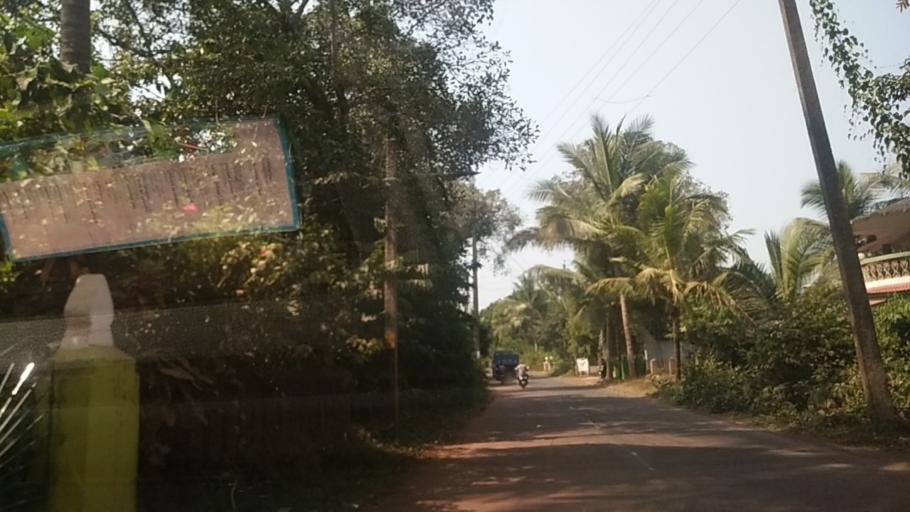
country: IN
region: Goa
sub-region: North Goa
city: Mapuca
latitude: 15.6152
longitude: 73.7993
